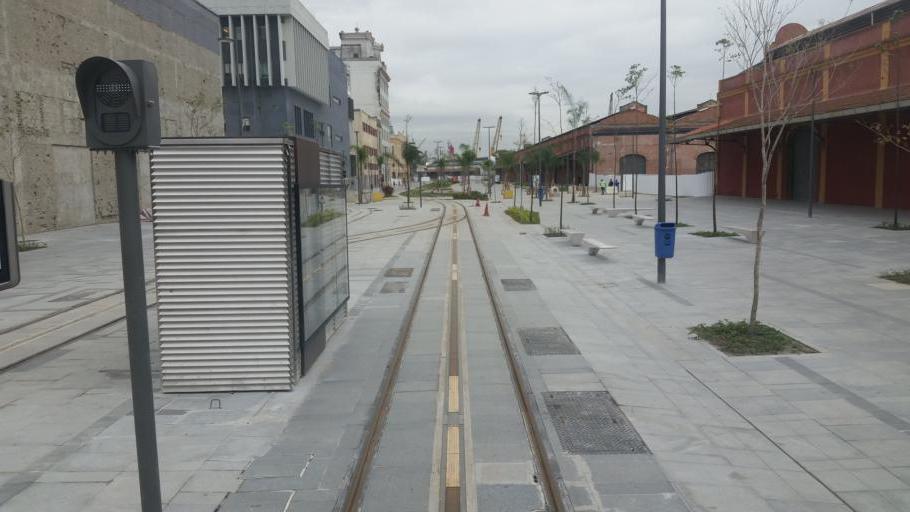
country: BR
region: Rio de Janeiro
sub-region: Rio De Janeiro
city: Rio de Janeiro
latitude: -22.8941
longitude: -43.1874
